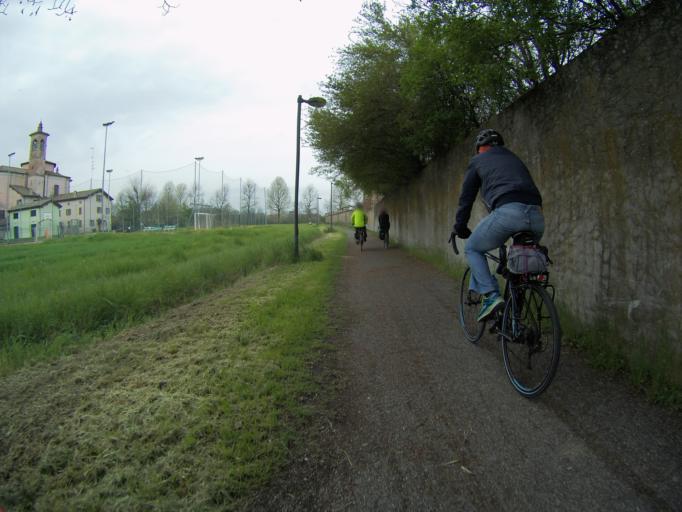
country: IT
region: Emilia-Romagna
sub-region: Provincia di Reggio Emilia
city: Codemondo-Quaresimo
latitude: 44.6814
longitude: 10.5922
